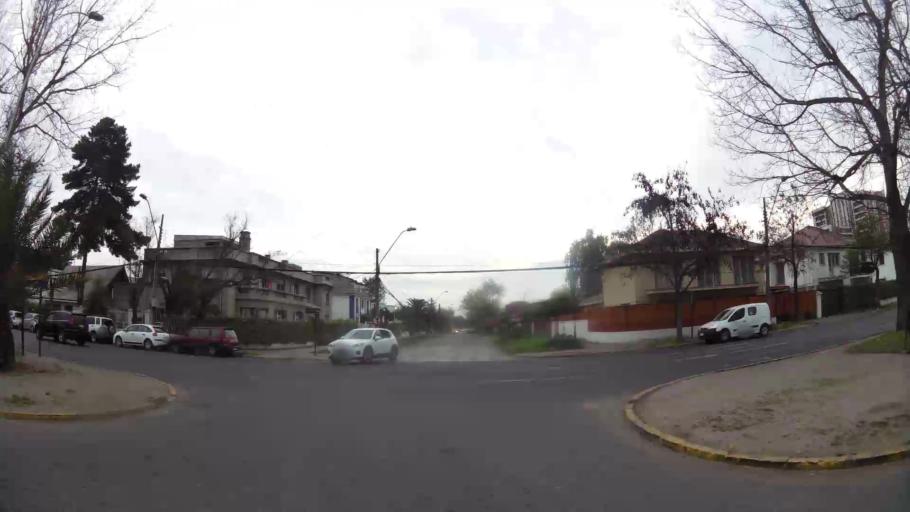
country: CL
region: Santiago Metropolitan
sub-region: Provincia de Santiago
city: Villa Presidente Frei, Nunoa, Santiago, Chile
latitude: -33.4585
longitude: -70.6096
